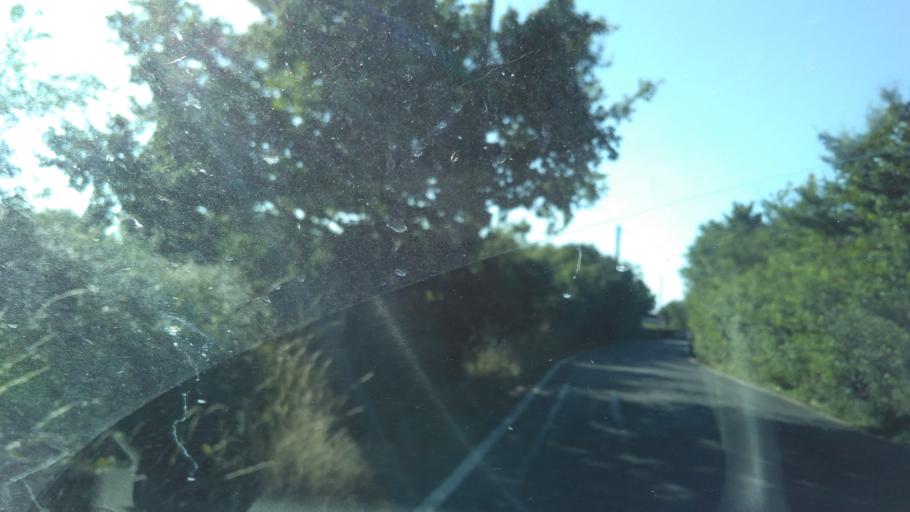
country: GB
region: England
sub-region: Kent
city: Whitstable
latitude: 51.3401
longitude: 1.0071
